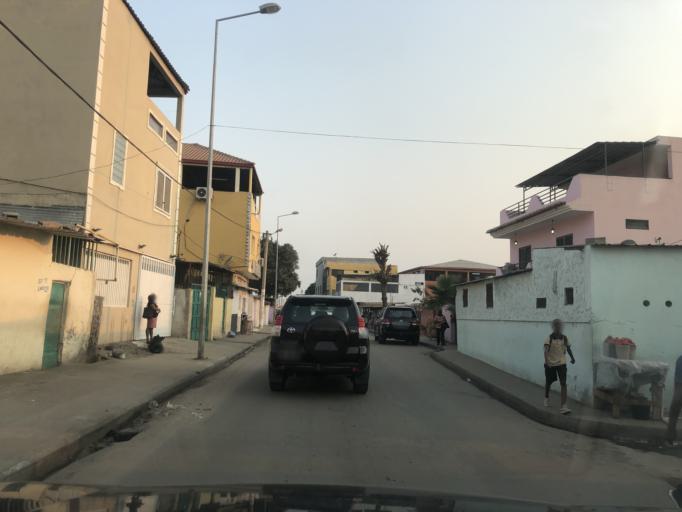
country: AO
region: Luanda
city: Luanda
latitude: -8.8435
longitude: 13.2250
